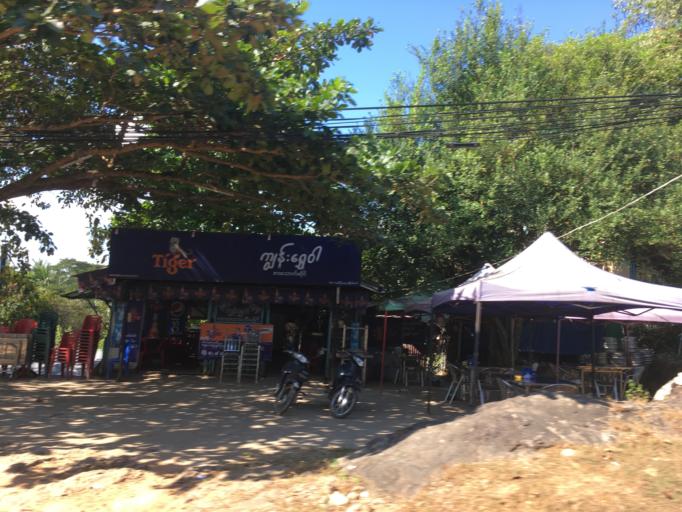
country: MM
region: Mon
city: Mawlamyine
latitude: 16.4686
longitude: 97.6310
